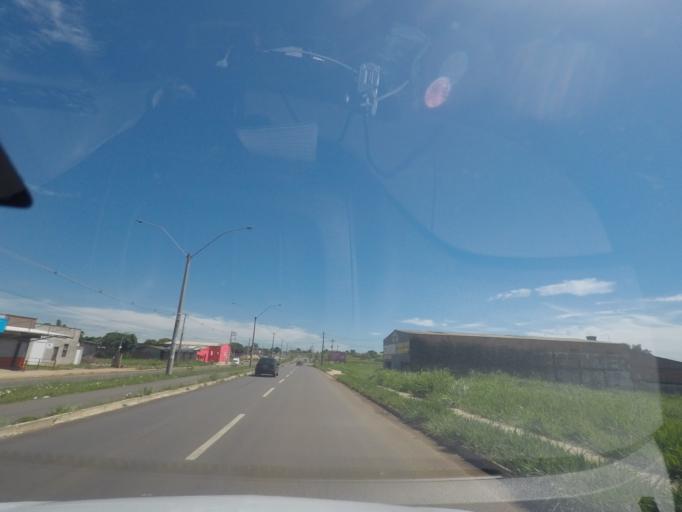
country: BR
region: Goias
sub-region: Aparecida De Goiania
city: Aparecida de Goiania
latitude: -16.7979
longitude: -49.3288
